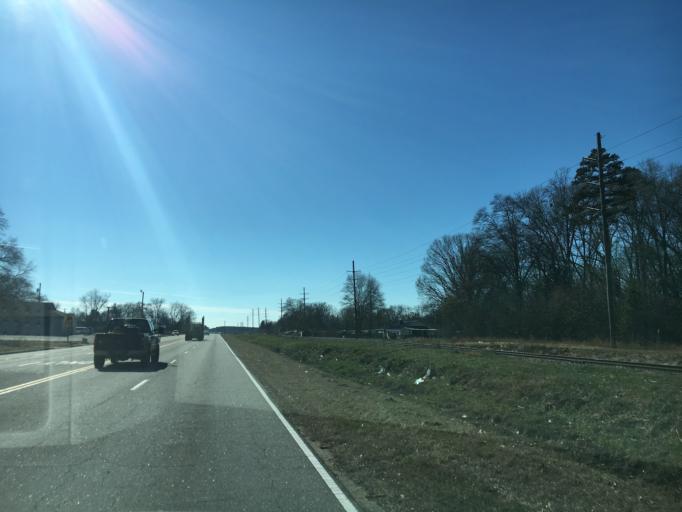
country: US
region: South Carolina
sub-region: Anderson County
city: Homeland Park
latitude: 34.4654
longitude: -82.6602
